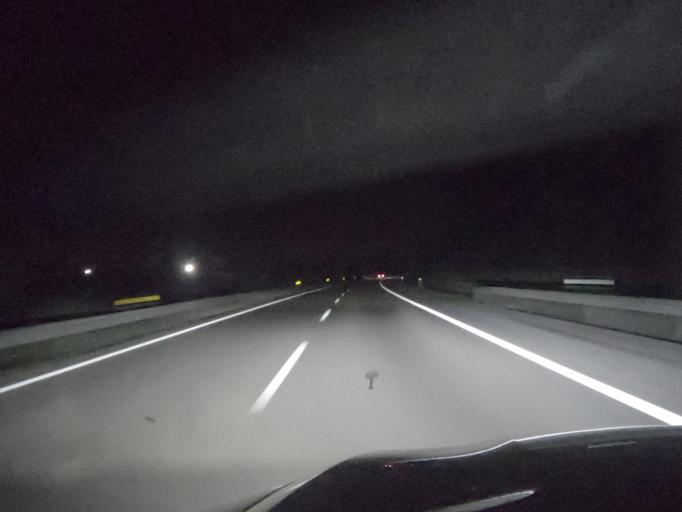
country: PT
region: Aveiro
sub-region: Oliveira do Bairro
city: Oliveira do Bairro
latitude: 40.4696
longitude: -8.5215
